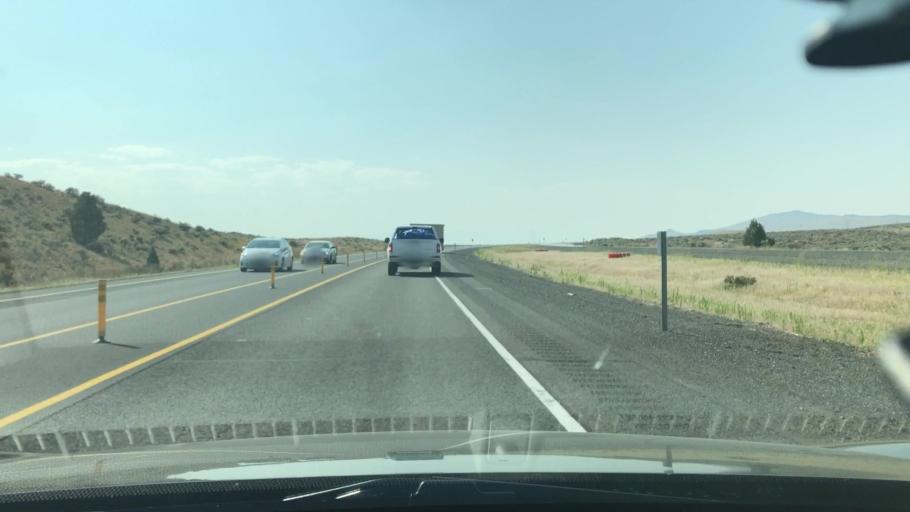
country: US
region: Oregon
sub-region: Baker County
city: Baker City
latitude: 44.6878
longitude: -117.6800
